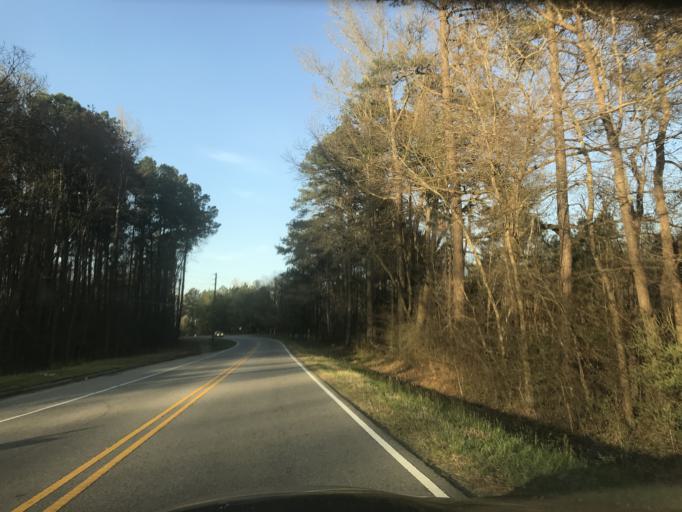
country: US
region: North Carolina
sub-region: Wake County
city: Knightdale
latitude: 35.7457
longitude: -78.5360
